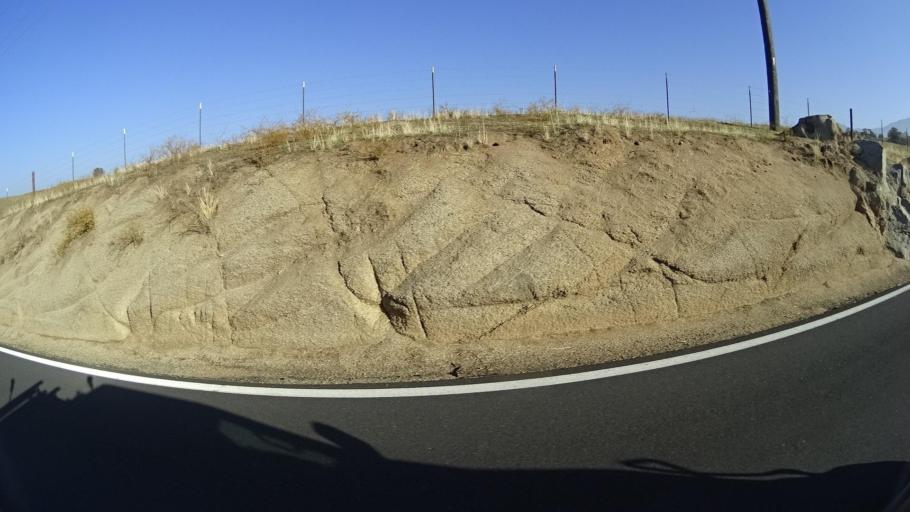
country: US
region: California
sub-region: Tulare County
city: Richgrove
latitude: 35.7415
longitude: -118.8744
